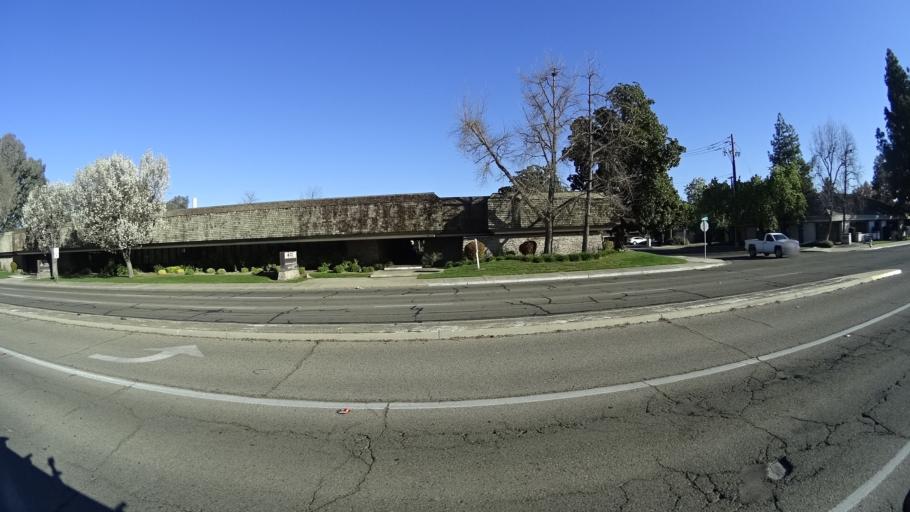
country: US
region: California
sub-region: Fresno County
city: Fresno
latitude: 36.8082
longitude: -119.8155
